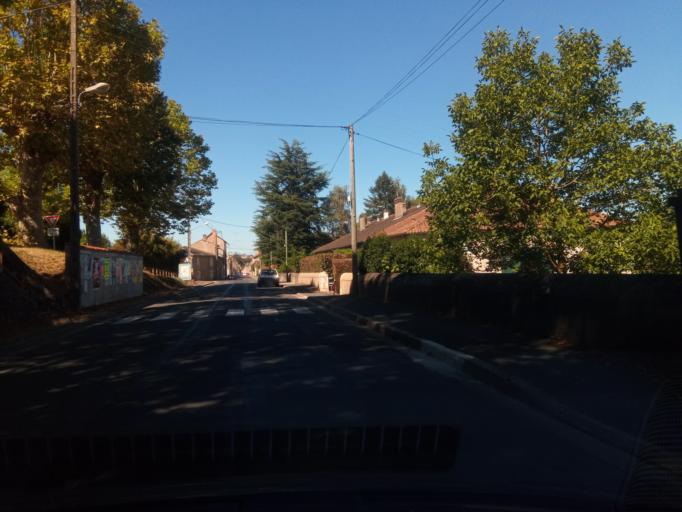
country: FR
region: Poitou-Charentes
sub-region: Departement de la Vienne
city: Montmorillon
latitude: 46.4178
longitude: 0.8741
